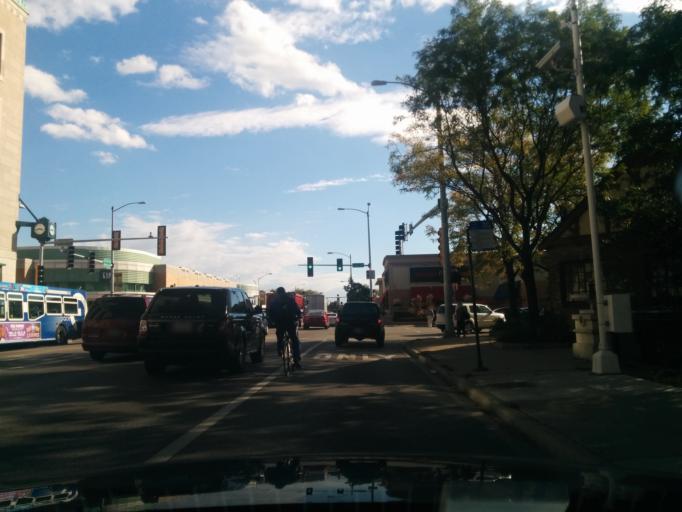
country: US
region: Illinois
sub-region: Cook County
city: River Forest
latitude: 41.8889
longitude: -87.8051
